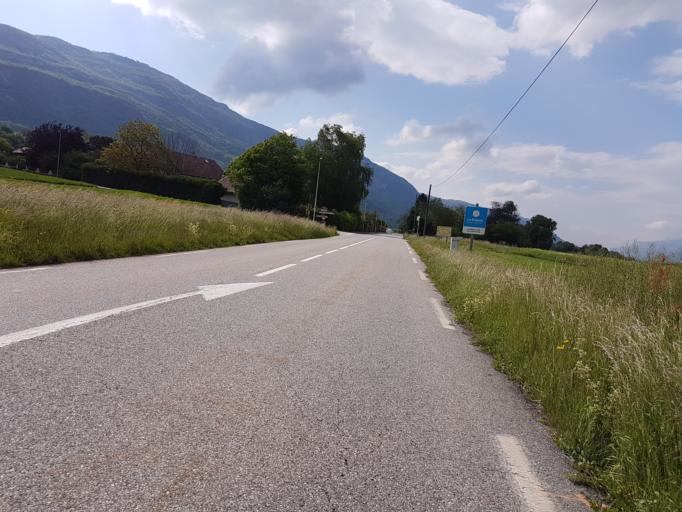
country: FR
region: Rhone-Alpes
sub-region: Departement de l'Ain
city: Culoz
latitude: 45.9306
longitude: 5.8298
